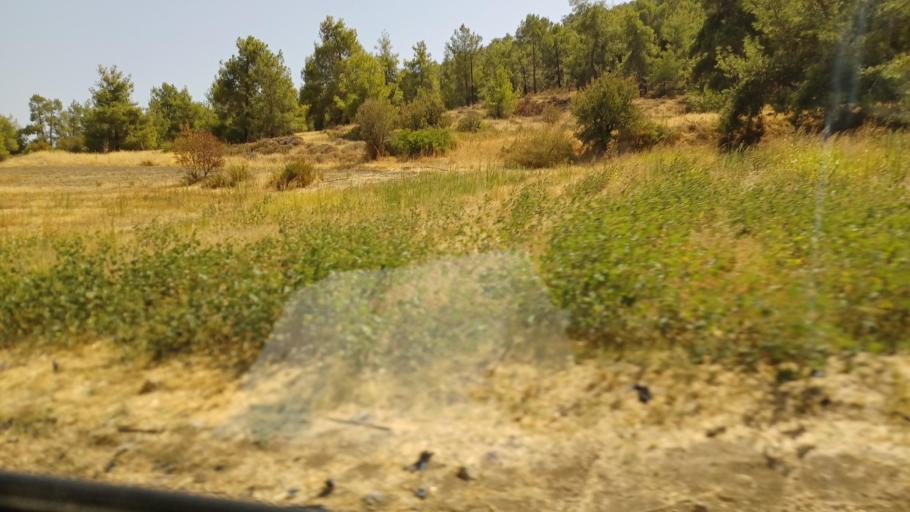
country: CY
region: Lefkosia
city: Lefka
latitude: 35.0580
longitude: 32.8947
